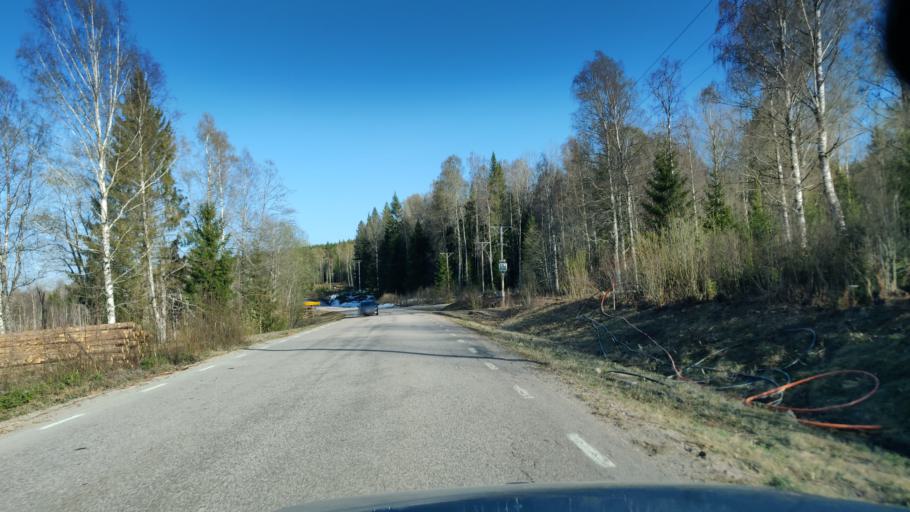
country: SE
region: Vaermland
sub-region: Munkfors Kommun
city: Munkfors
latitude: 59.9701
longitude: 13.4203
